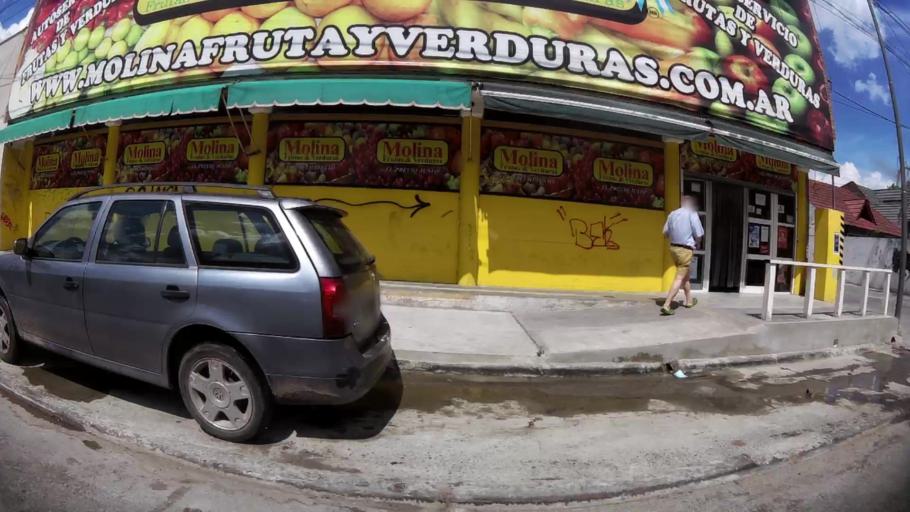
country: AR
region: Buenos Aires
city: Ituzaingo
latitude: -34.6479
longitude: -58.6579
